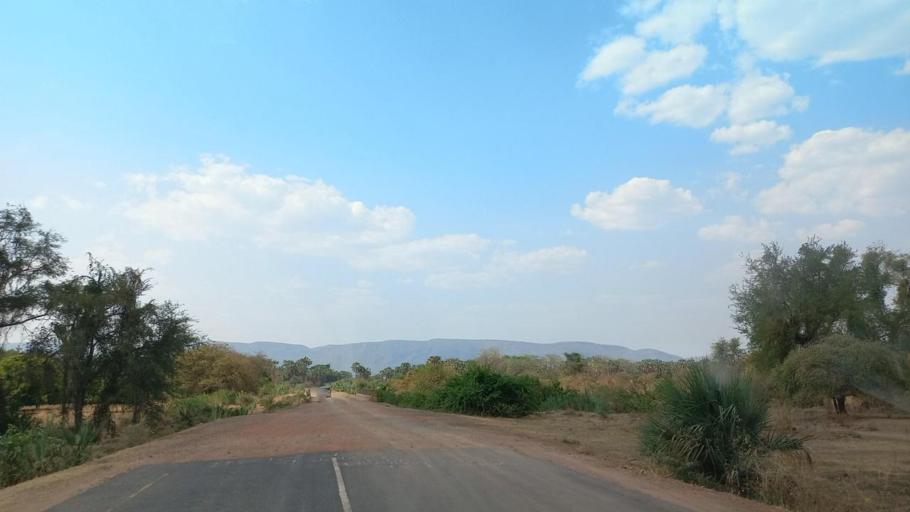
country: ZM
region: Lusaka
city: Luangwa
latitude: -15.0944
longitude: 30.1928
